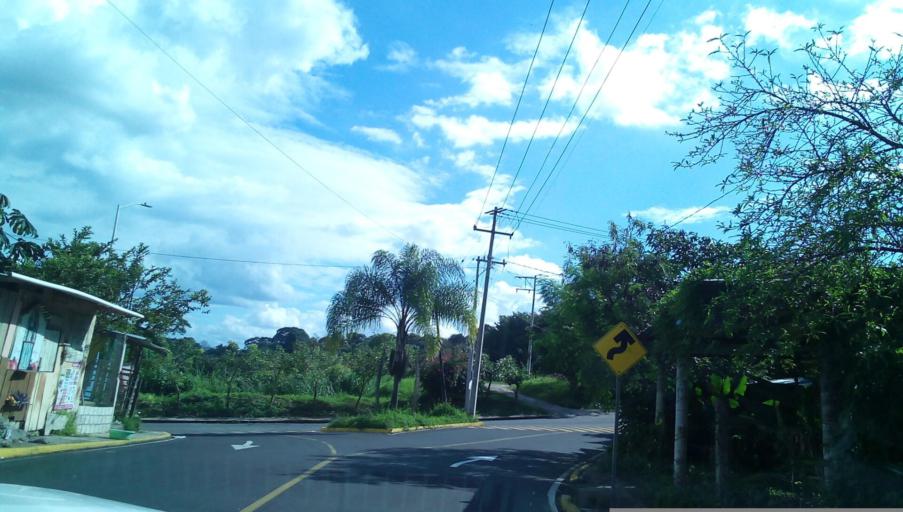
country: MX
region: Veracruz
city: Cordoba
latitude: 18.8935
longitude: -96.9196
